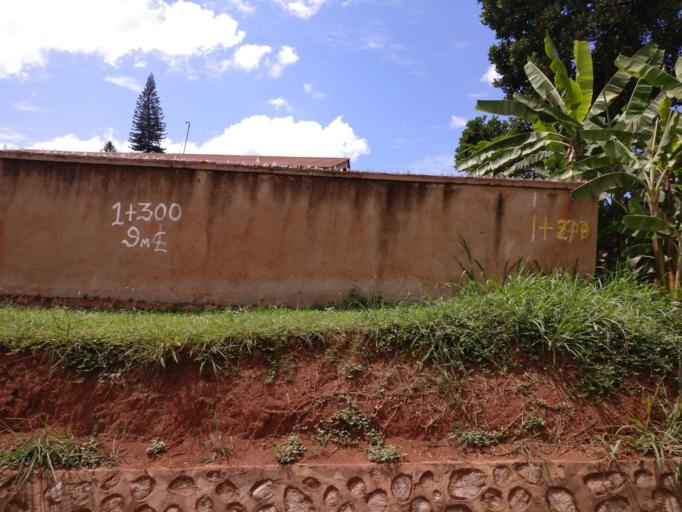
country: UG
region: Central Region
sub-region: Kampala District
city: Kampala
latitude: 0.2819
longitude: 32.5627
